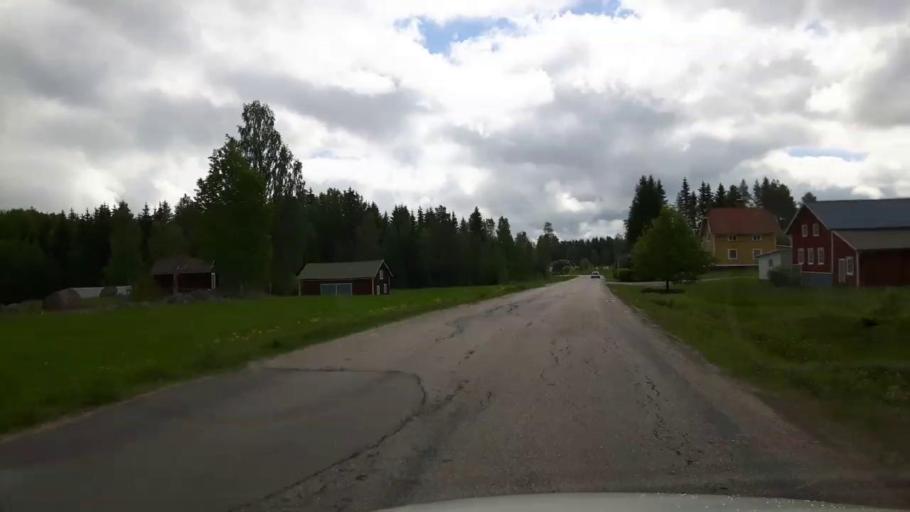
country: SE
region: Gaevleborg
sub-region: Ovanakers Kommun
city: Edsbyn
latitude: 61.3428
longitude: 15.9359
